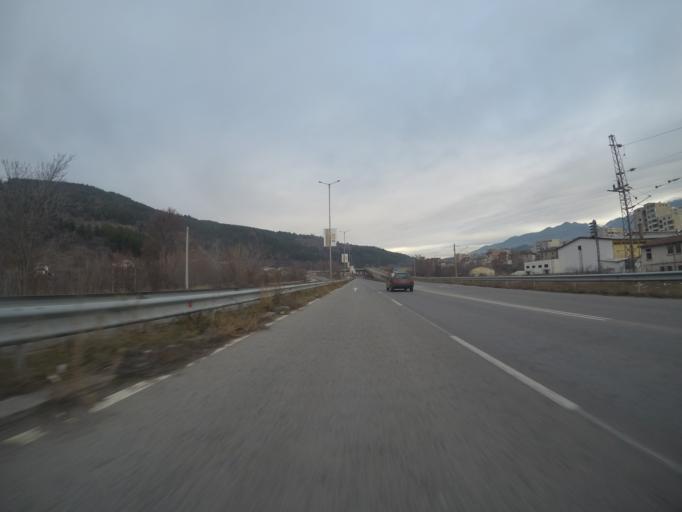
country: BG
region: Kyustendil
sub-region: Obshtina Dupnitsa
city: Dupnitsa
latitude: 42.2666
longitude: 23.1075
